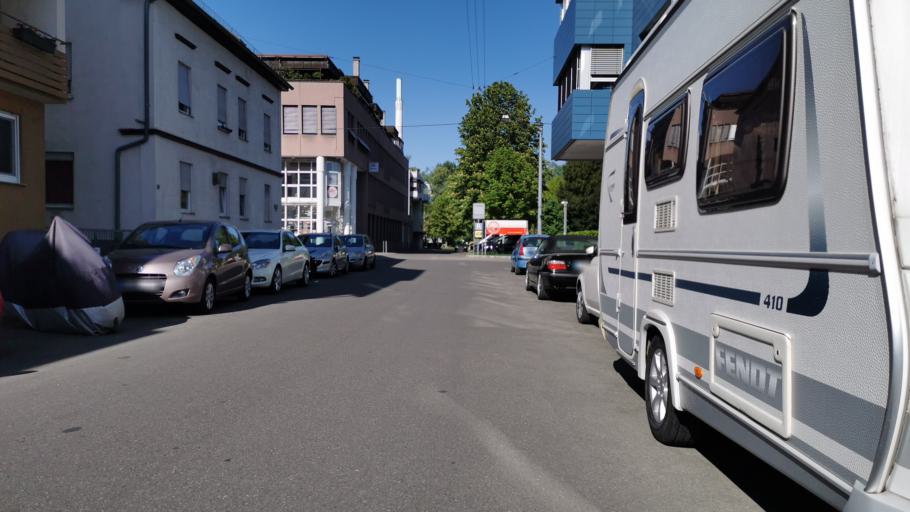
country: DE
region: Baden-Wuerttemberg
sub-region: Regierungsbezirk Stuttgart
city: Stuttgart-Ost
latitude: 48.8099
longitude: 9.2130
